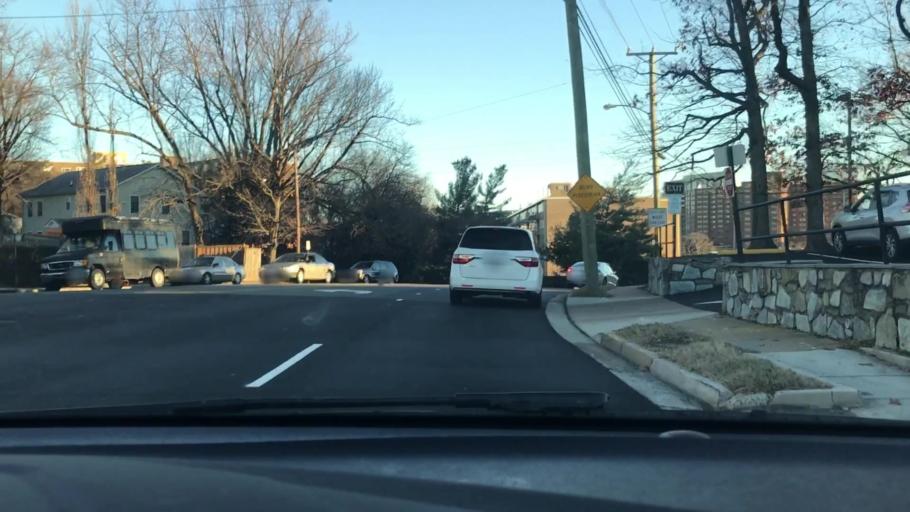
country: US
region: Virginia
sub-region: Fairfax County
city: Baileys Crossroads
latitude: 38.8550
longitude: -77.1229
